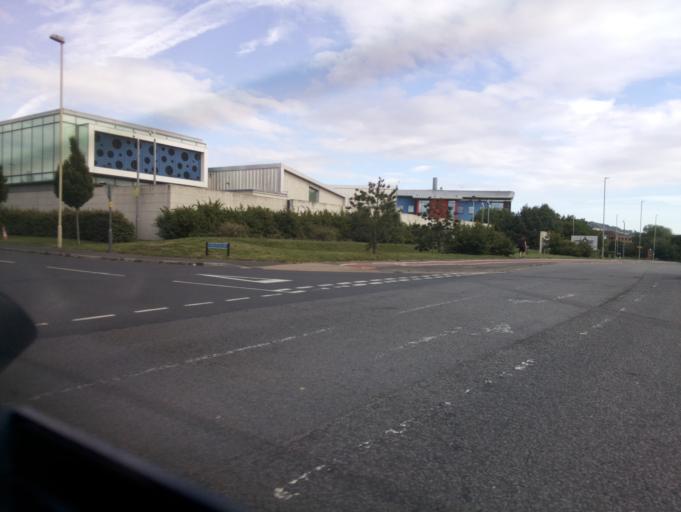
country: GB
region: England
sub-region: Gloucestershire
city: Gloucester
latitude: 51.8157
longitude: -2.2773
